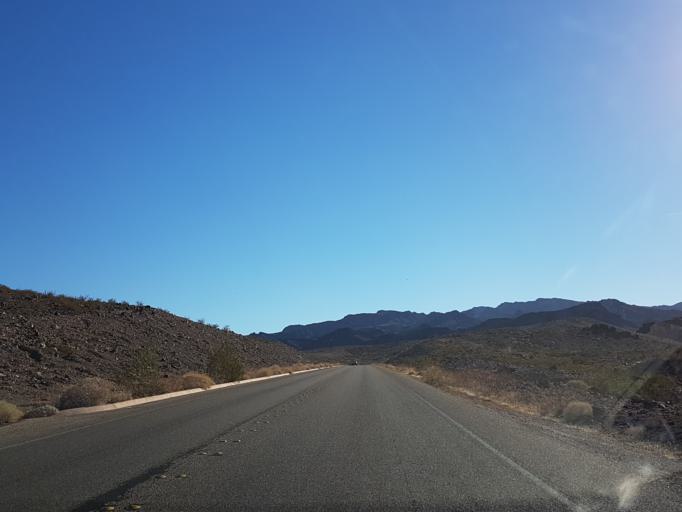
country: US
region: Nevada
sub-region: Clark County
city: Boulder City
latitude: 36.0884
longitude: -114.8262
